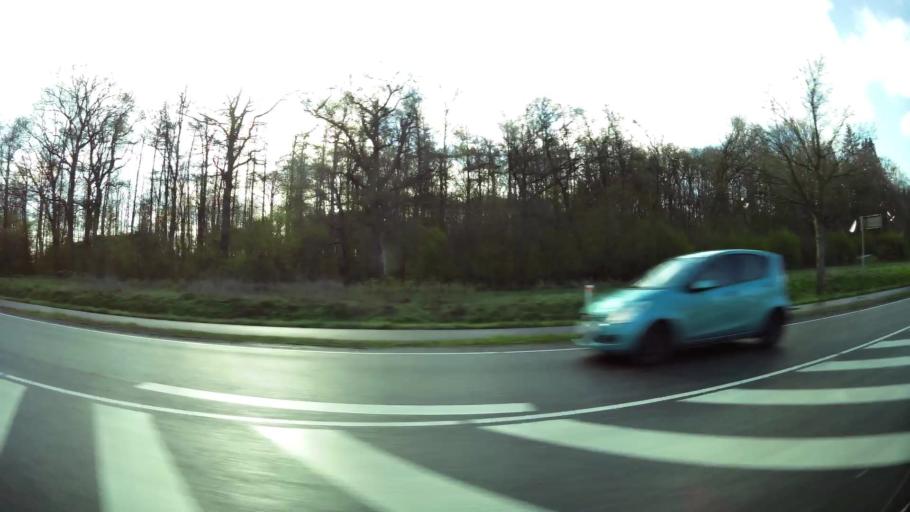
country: DK
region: Zealand
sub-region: Lejre Kommune
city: Osted
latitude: 55.5398
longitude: 11.9279
